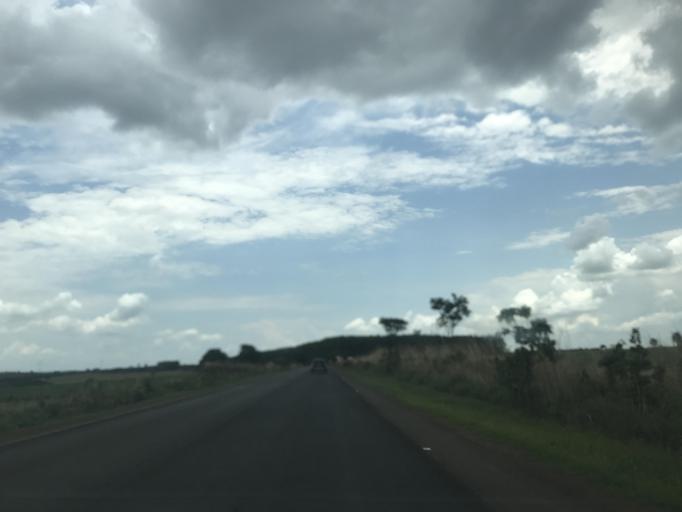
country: BR
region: Goias
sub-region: Vianopolis
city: Vianopolis
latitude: -16.9221
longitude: -48.5568
